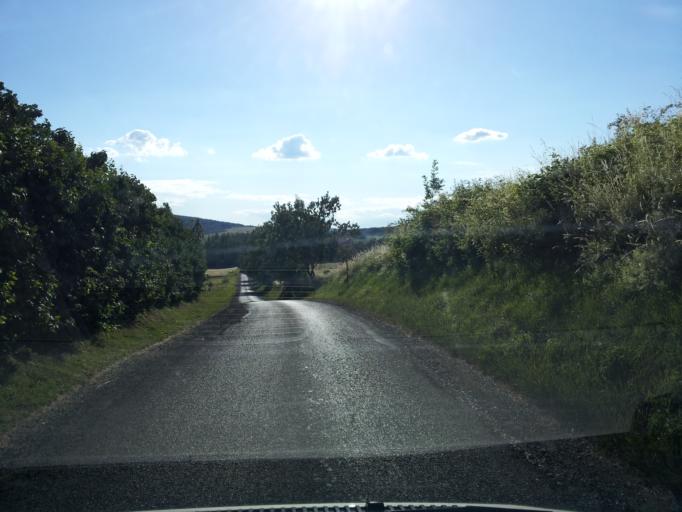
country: HU
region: Veszprem
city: Zirc
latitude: 47.2068
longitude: 17.8568
